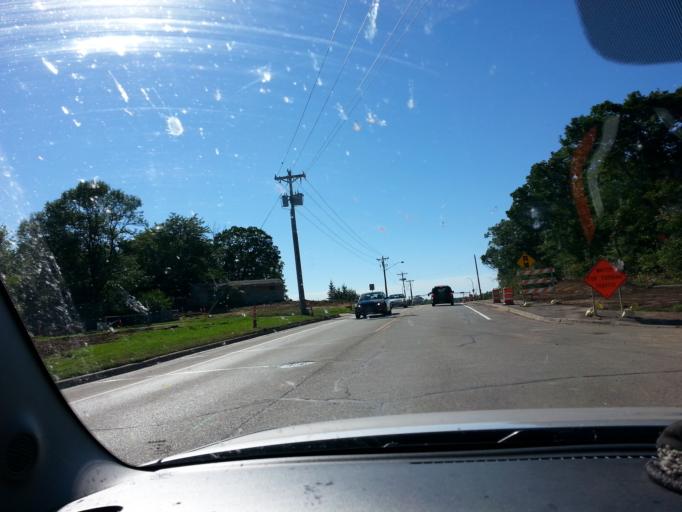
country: US
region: Minnesota
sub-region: Dakota County
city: Lakeville
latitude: 44.6814
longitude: -93.2745
